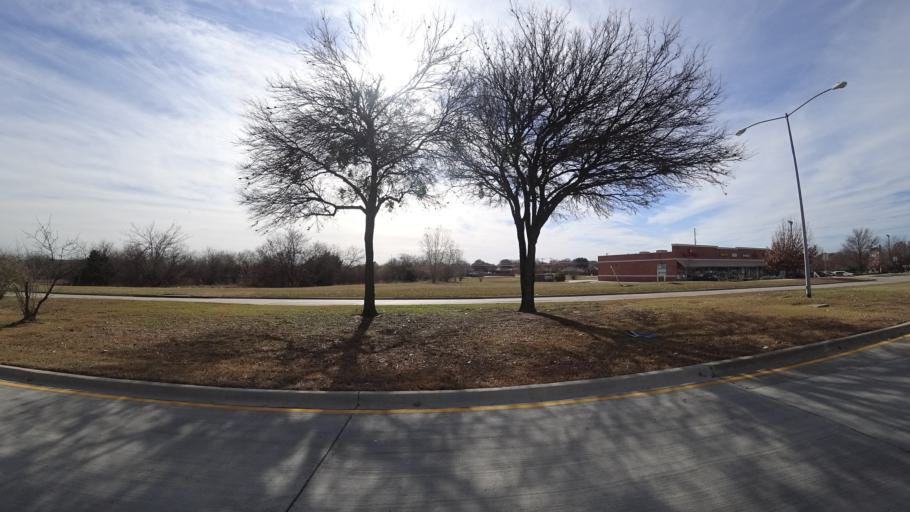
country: US
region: Texas
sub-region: Denton County
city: Highland Village
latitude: 33.0633
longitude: -97.0336
